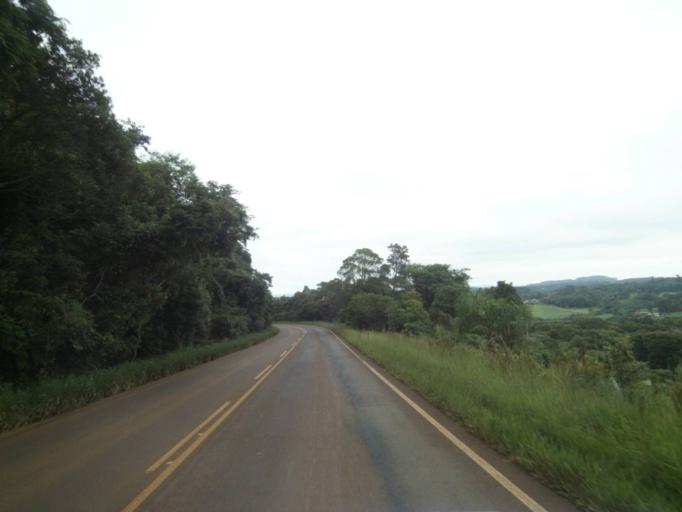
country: BR
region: Parana
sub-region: Pitanga
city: Pitanga
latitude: -24.9172
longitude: -51.8705
